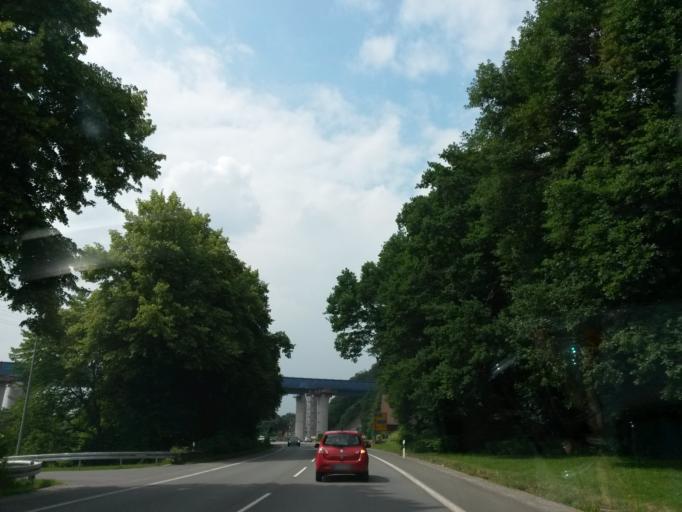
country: DE
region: North Rhine-Westphalia
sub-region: Regierungsbezirk Arnsberg
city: Hagen
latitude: 51.3859
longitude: 7.5284
